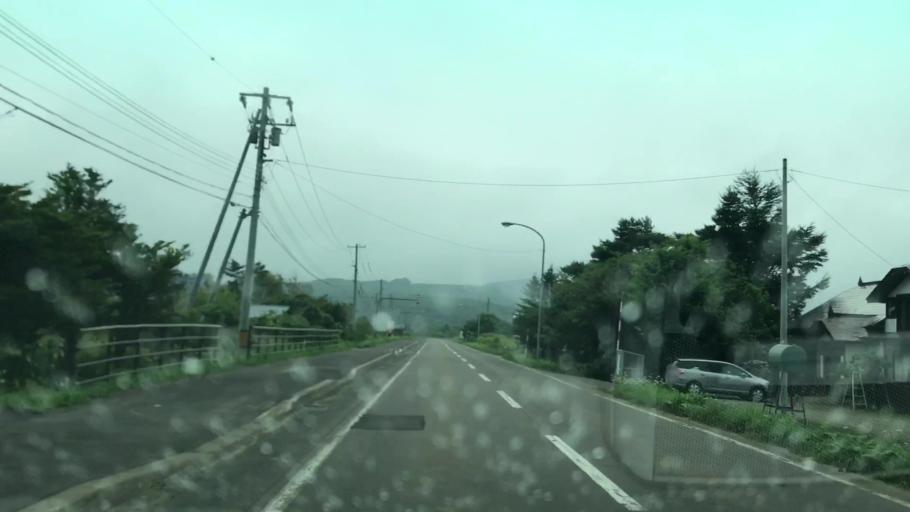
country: JP
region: Hokkaido
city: Iwanai
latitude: 42.7540
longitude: 140.2788
